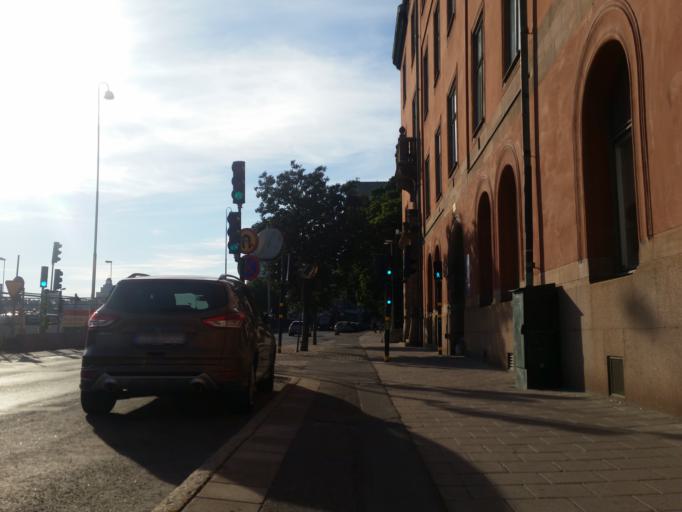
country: SE
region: Stockholm
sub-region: Stockholms Kommun
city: Stockholm
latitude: 59.3366
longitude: 18.0463
